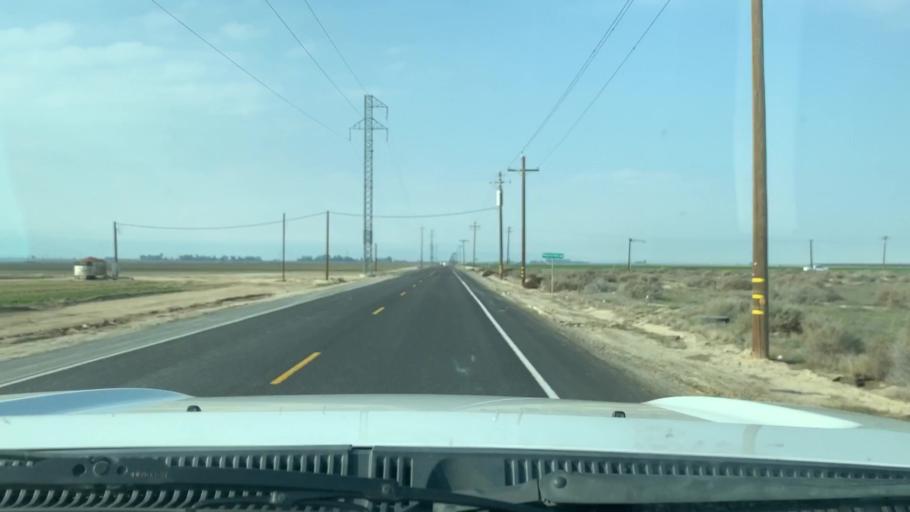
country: US
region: California
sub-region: Kern County
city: Shafter
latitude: 35.4421
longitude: -119.3661
